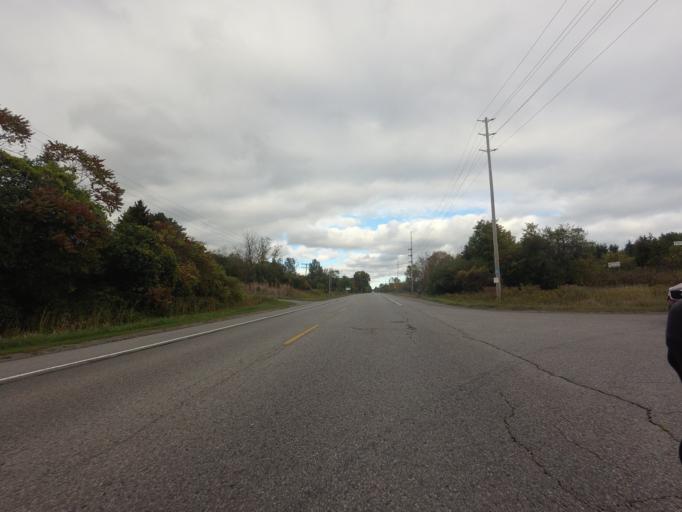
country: CA
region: Ontario
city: Cobourg
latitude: 43.9736
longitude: -78.1068
